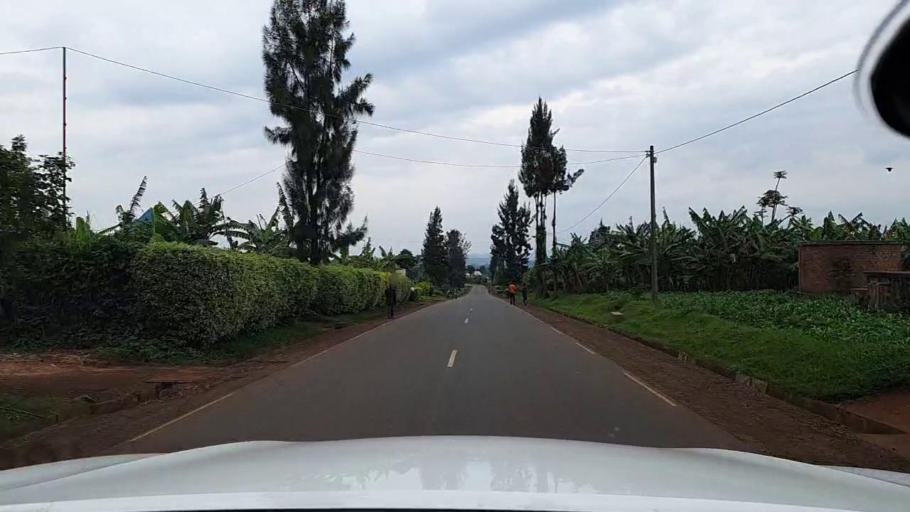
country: RW
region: Western Province
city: Cyangugu
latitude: -2.6003
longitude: 28.9328
